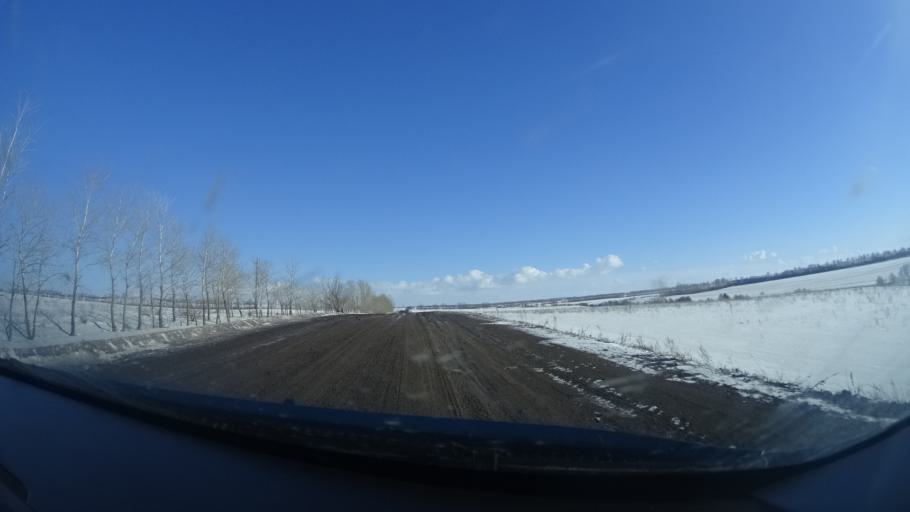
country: RU
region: Bashkortostan
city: Chishmy
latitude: 54.6012
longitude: 55.2235
